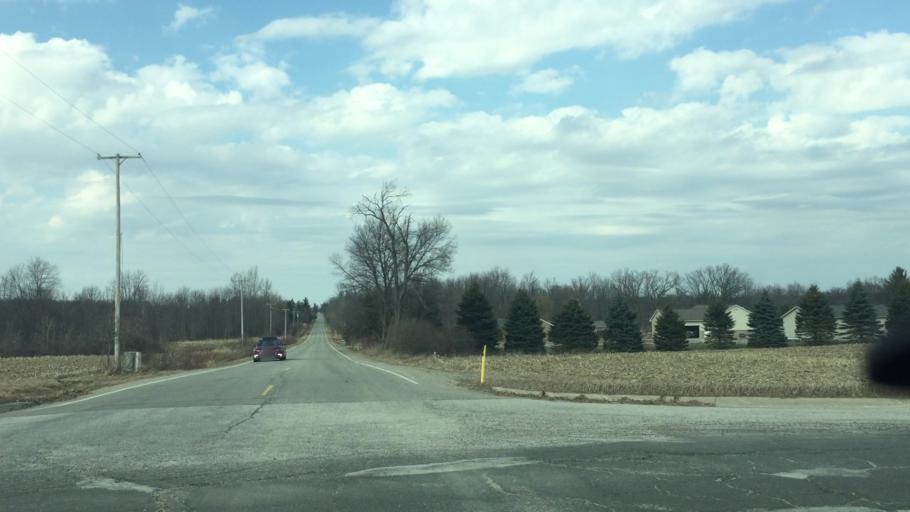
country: US
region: Michigan
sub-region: Lapeer County
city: Lapeer
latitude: 43.0006
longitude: -83.2819
